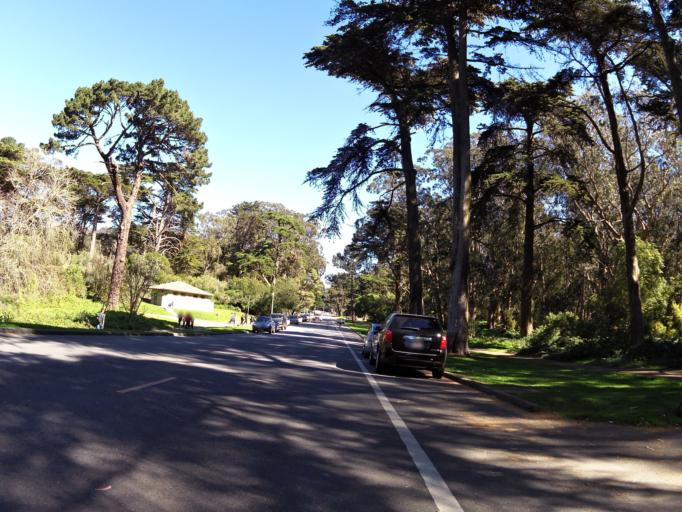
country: US
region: California
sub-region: San Mateo County
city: Daly City
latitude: 37.7675
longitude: -122.5026
